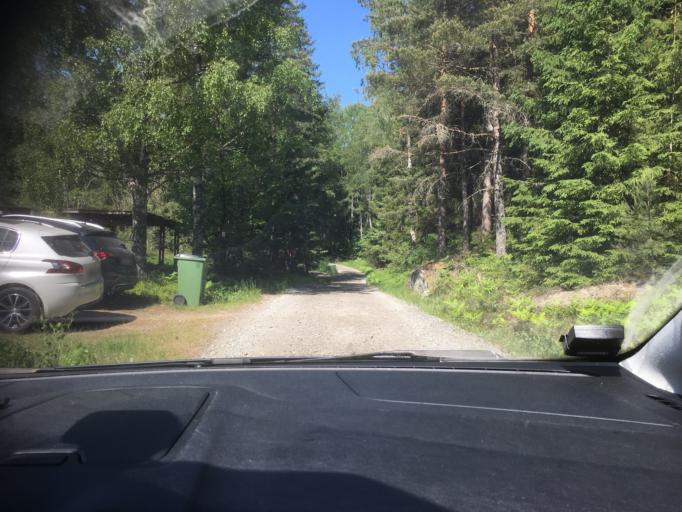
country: SE
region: Stockholm
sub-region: Haninge Kommun
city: Jordbro
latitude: 59.0135
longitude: 18.1652
